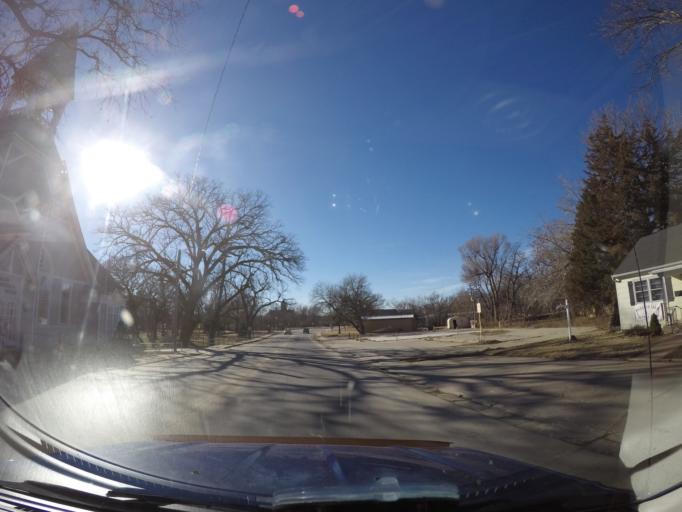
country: US
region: Kansas
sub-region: Marion County
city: Marion
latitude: 38.3486
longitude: -97.0160
